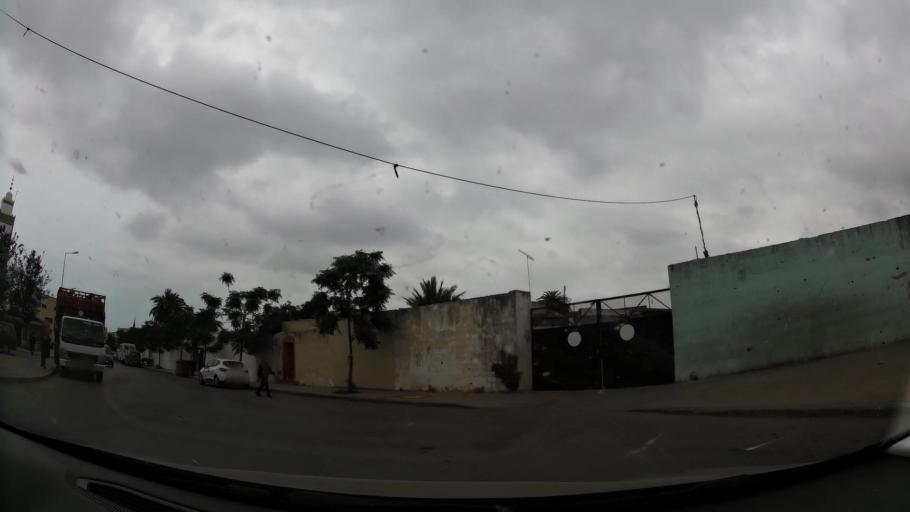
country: MA
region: Rabat-Sale-Zemmour-Zaer
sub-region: Rabat
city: Rabat
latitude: 33.9975
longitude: -6.8145
